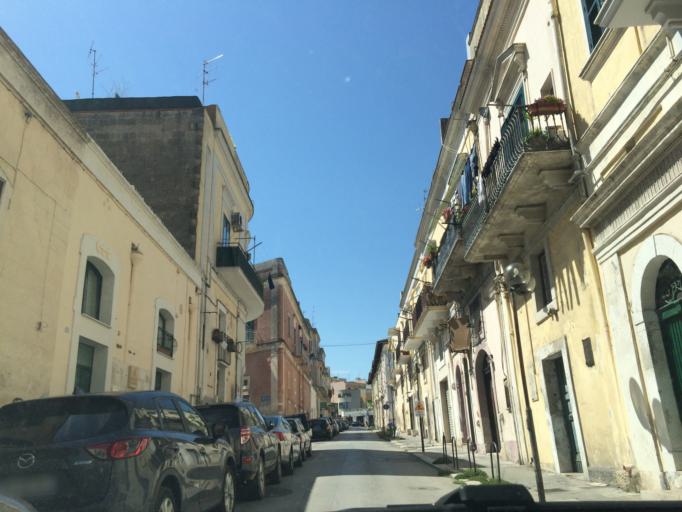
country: IT
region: Basilicate
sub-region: Provincia di Matera
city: Matera
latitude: 40.6704
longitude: 16.6081
